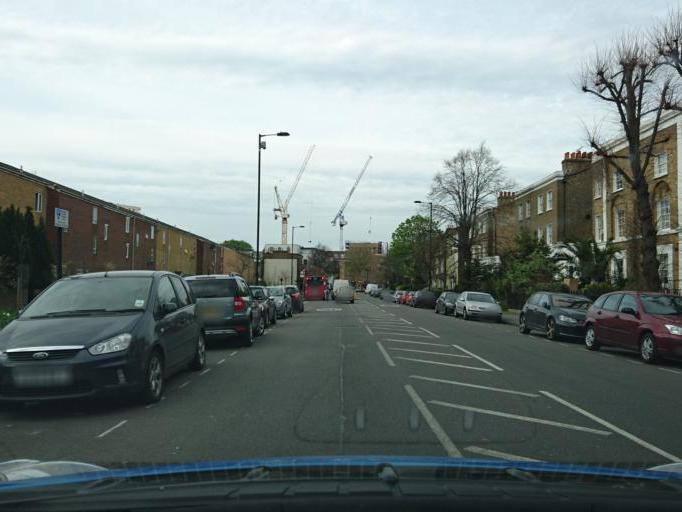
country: GB
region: England
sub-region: Greater London
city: Bethnal Green
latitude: 51.5445
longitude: -0.0699
